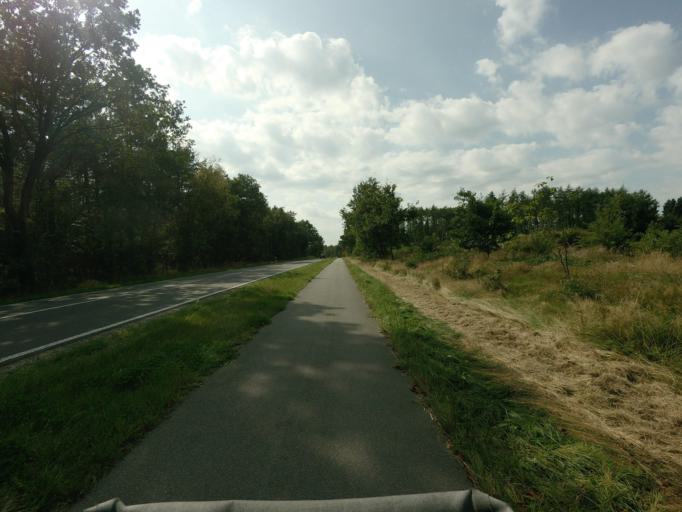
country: DE
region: Lower Saxony
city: Wielen
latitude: 52.5302
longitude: 6.7320
